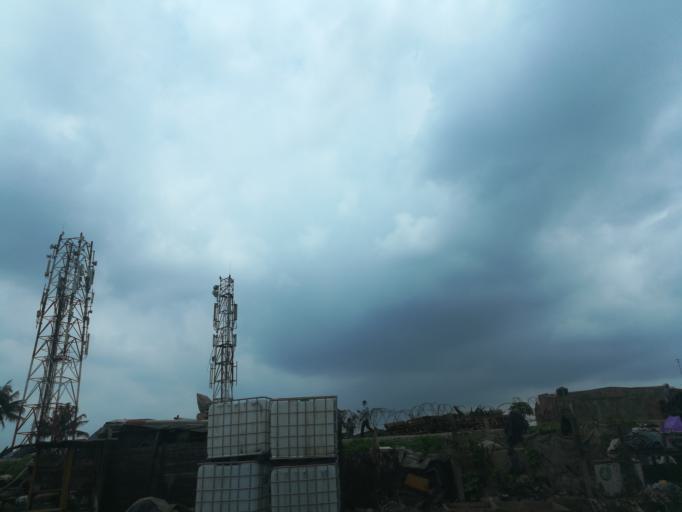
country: NG
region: Lagos
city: Agege
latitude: 6.6176
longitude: 3.3265
